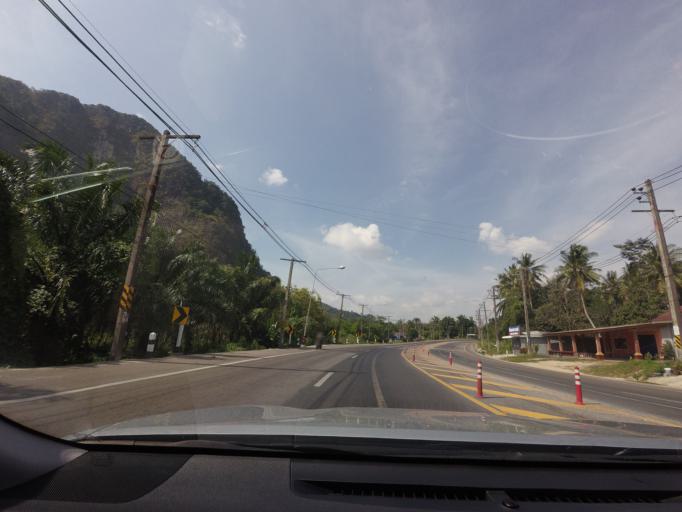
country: TH
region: Phangnga
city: Ban Ao Nang
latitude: 8.0814
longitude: 98.8040
